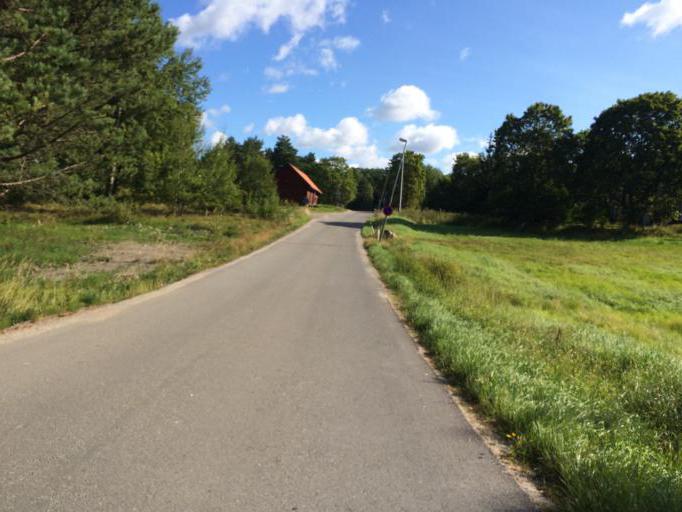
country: SE
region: Stockholm
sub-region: Haninge Kommun
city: Handen
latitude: 59.2226
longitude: 18.1008
